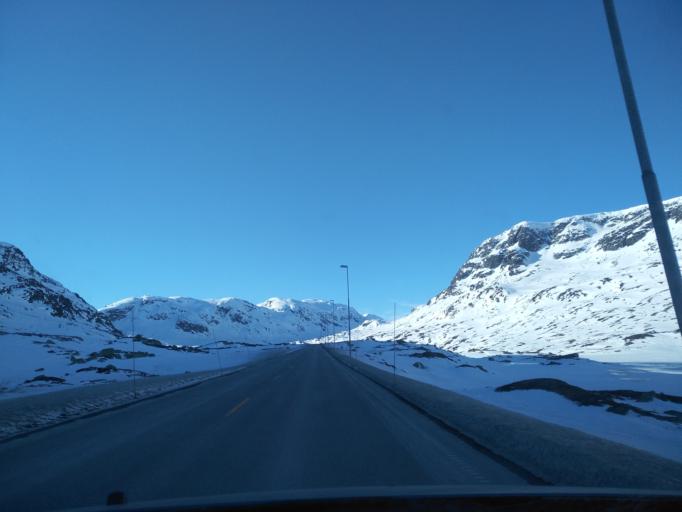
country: NO
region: Aust-Agder
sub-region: Bykle
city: Hovden
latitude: 59.8497
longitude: 7.1149
